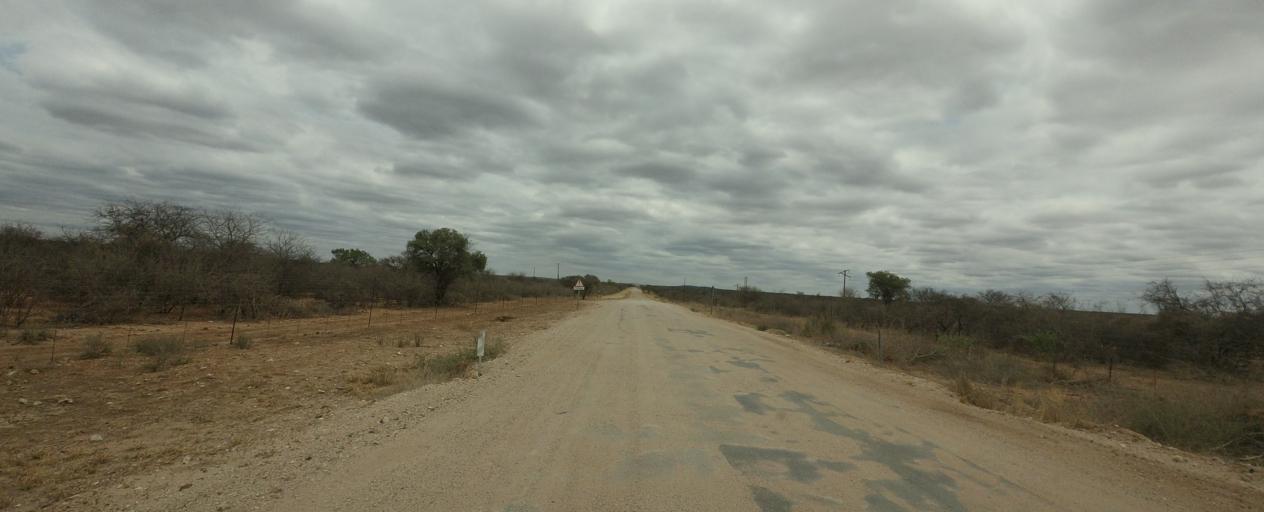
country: BW
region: Central
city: Mathathane
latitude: -22.7058
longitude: 28.5974
